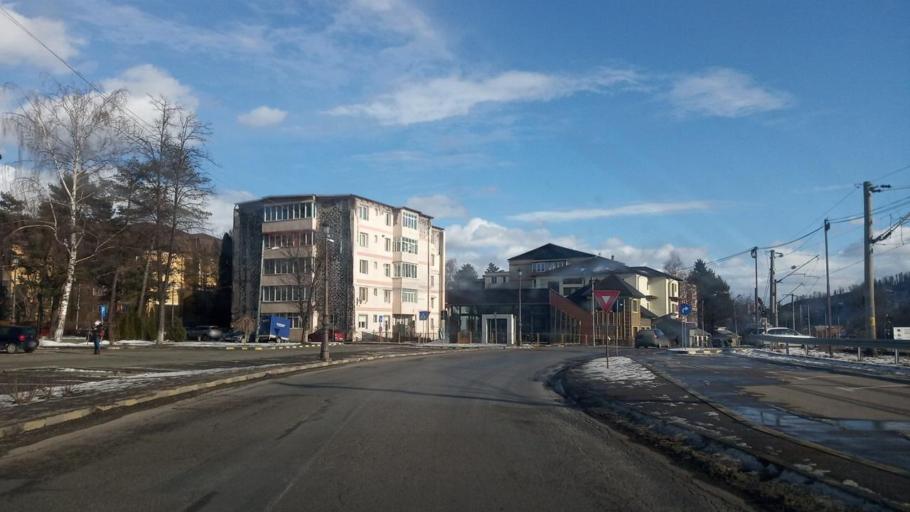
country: RO
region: Suceava
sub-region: Oras Gura Humorului
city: Gura Humorului
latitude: 47.5532
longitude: 25.8891
